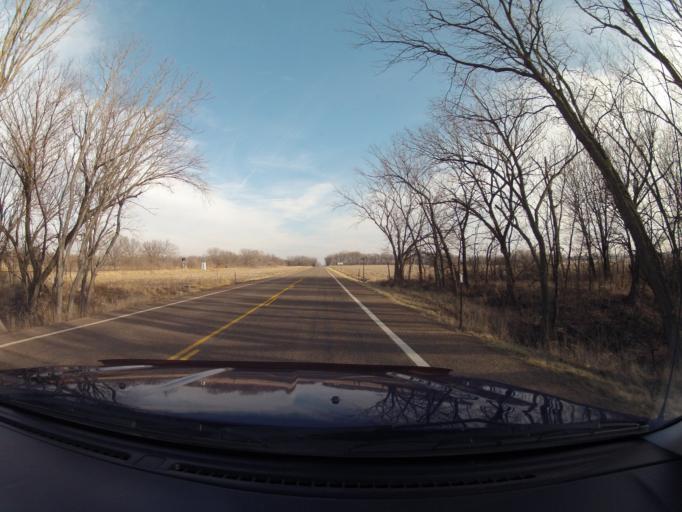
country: US
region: Kansas
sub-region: Pottawatomie County
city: Saint Marys
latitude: 39.2151
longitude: -96.1190
